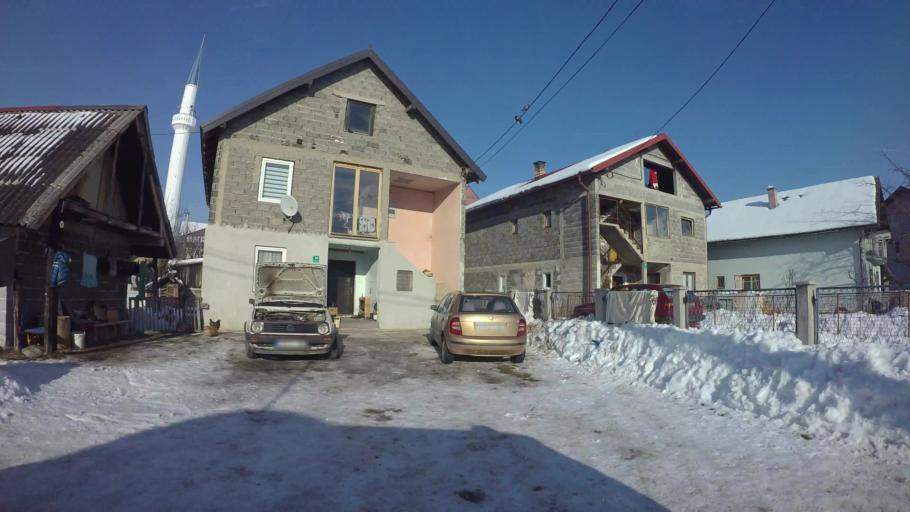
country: BA
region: Federation of Bosnia and Herzegovina
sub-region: Kanton Sarajevo
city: Sarajevo
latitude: 43.8084
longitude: 18.3281
